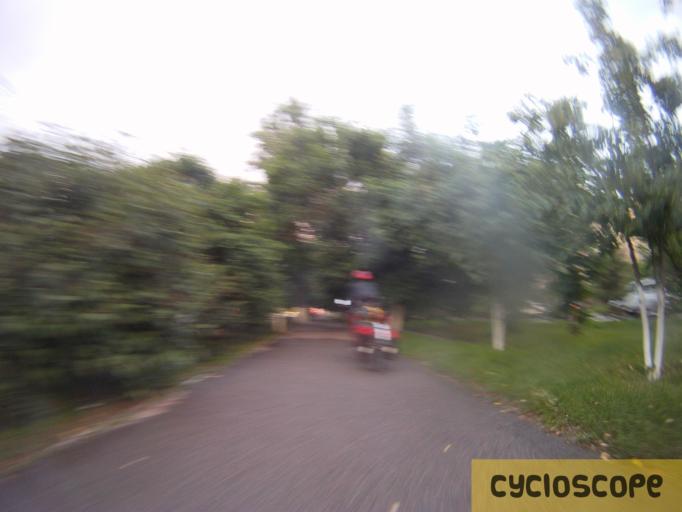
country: KZ
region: Almaty Qalasy
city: Almaty
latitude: 43.2227
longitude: 76.8485
